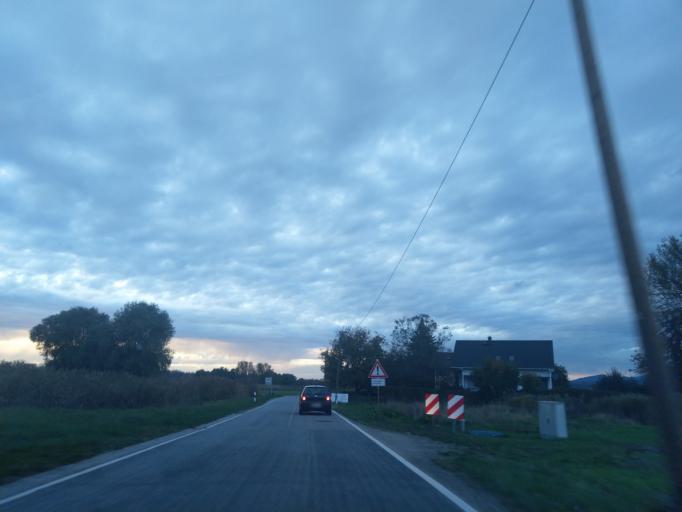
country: DE
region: Bavaria
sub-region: Lower Bavaria
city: Niederalteich
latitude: 48.7701
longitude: 13.0183
